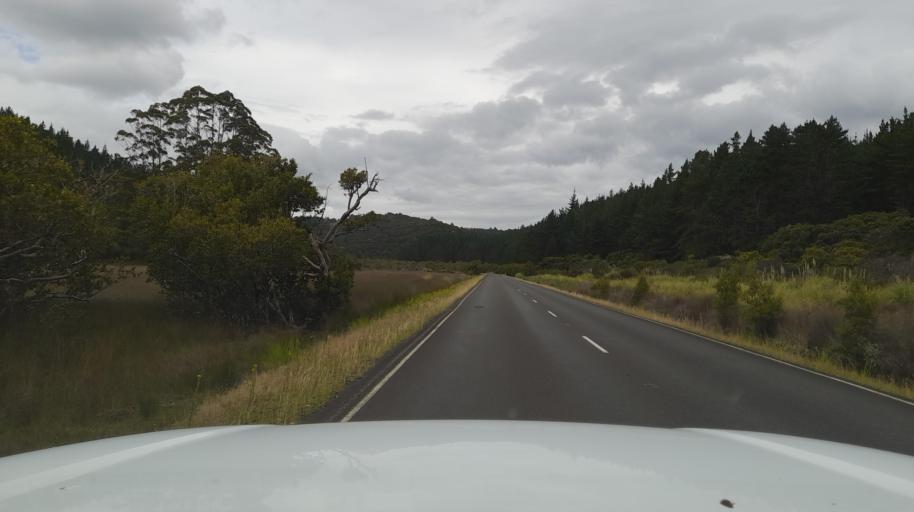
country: NZ
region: Northland
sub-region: Far North District
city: Kaitaia
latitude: -35.3634
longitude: 173.4361
